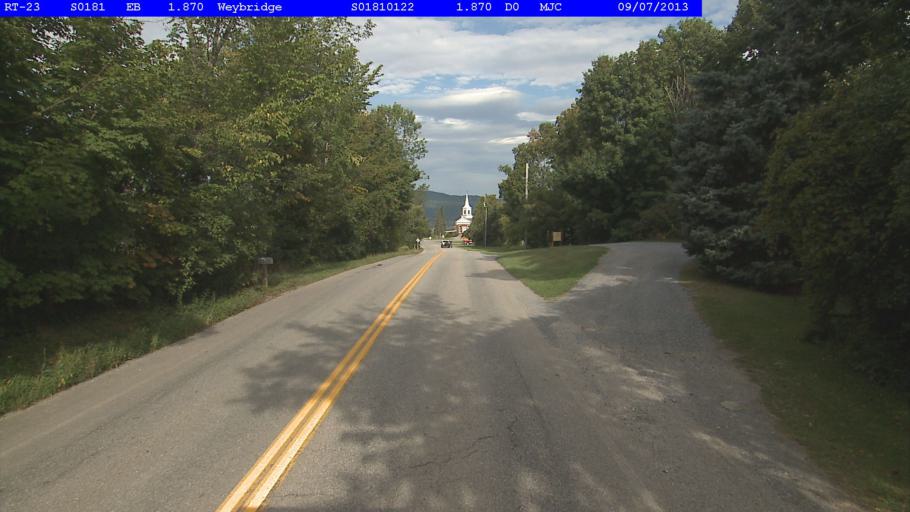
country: US
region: Vermont
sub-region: Addison County
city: Middlebury (village)
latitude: 44.0370
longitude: -73.2097
